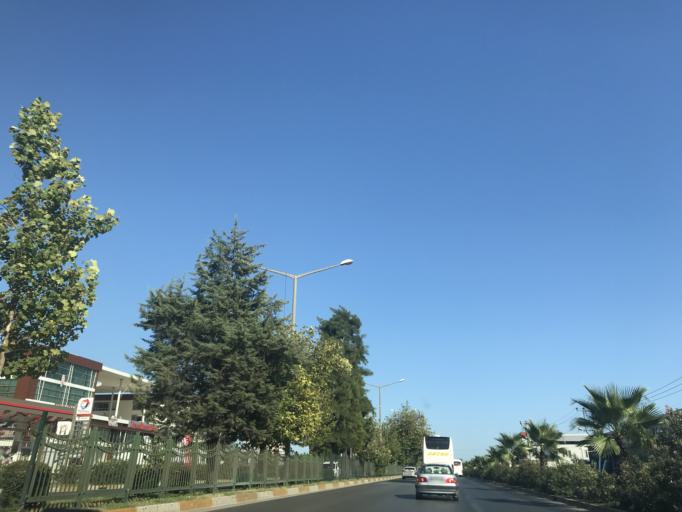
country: TR
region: Antalya
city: Antalya
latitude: 36.9047
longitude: 30.7536
